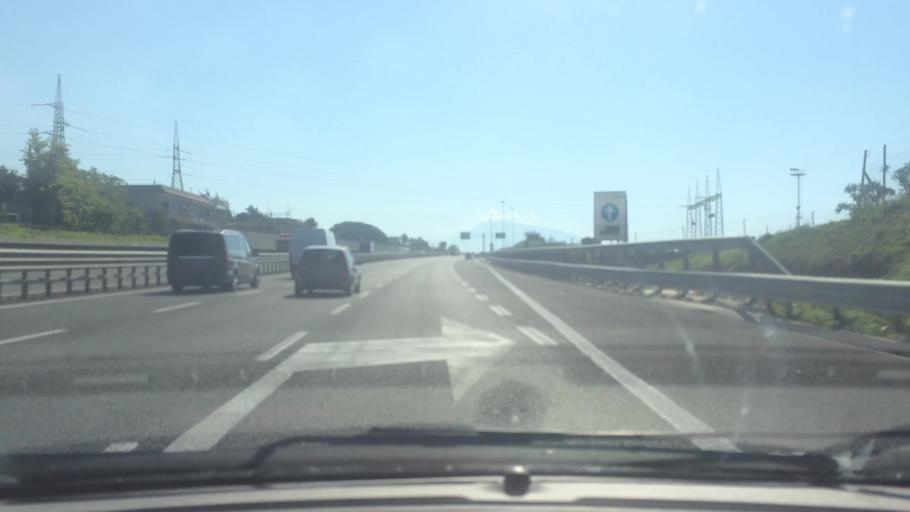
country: IT
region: Campania
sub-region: Provincia di Napoli
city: Ercolano
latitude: 40.8099
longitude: 14.3620
